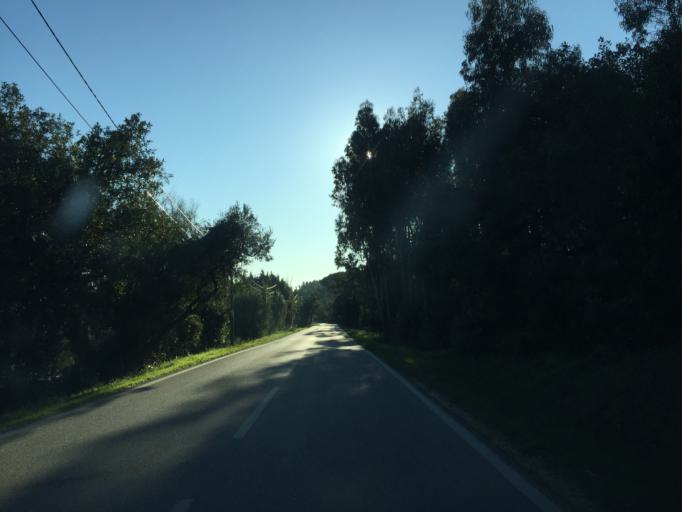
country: PT
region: Coimbra
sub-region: Figueira da Foz
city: Alhadas
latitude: 40.1741
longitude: -8.8023
